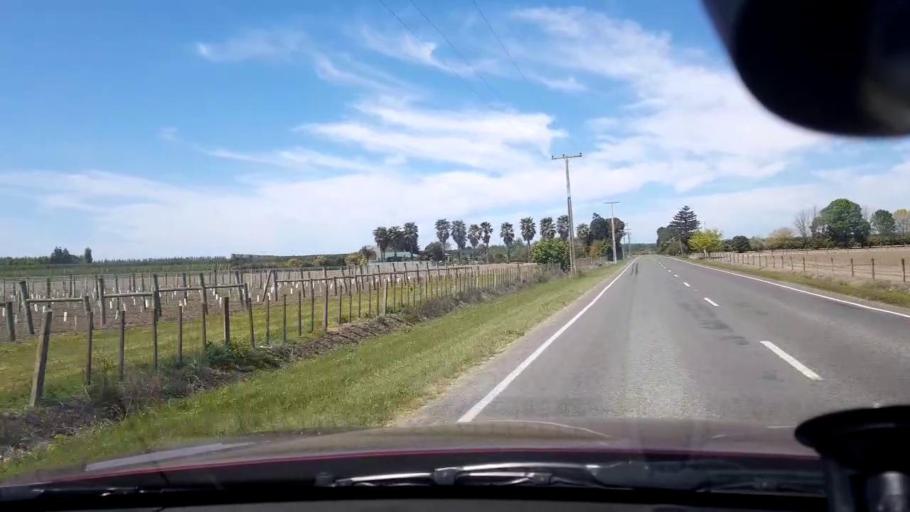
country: NZ
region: Gisborne
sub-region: Gisborne District
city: Gisborne
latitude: -38.6351
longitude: 177.9298
